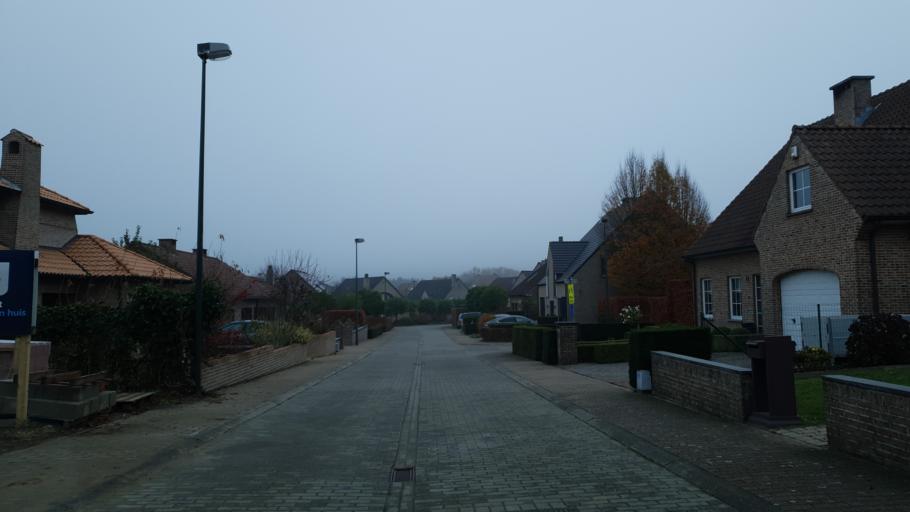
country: BE
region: Flanders
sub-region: Provincie Vlaams-Brabant
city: Kortenberg
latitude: 50.8807
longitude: 4.5304
